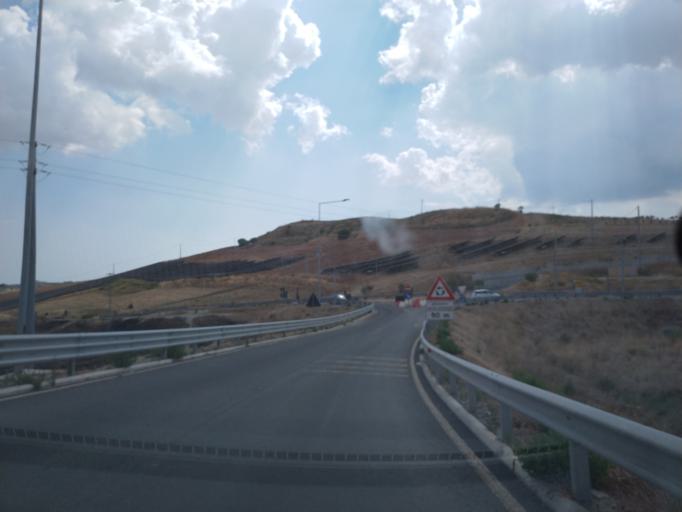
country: IT
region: Sicily
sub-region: Provincia di Caltanissetta
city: San Cataldo
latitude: 37.4491
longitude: 13.9718
